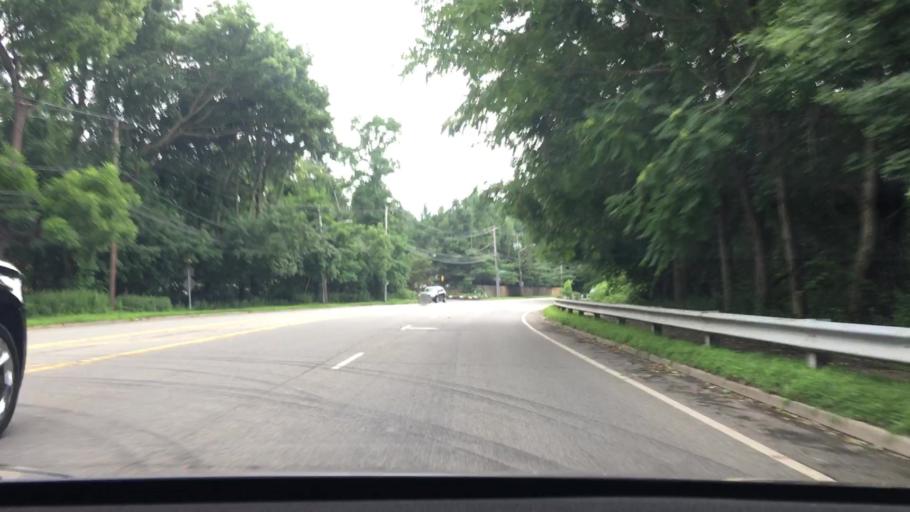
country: US
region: New York
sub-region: Nassau County
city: Woodbury
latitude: 40.8141
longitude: -73.4685
